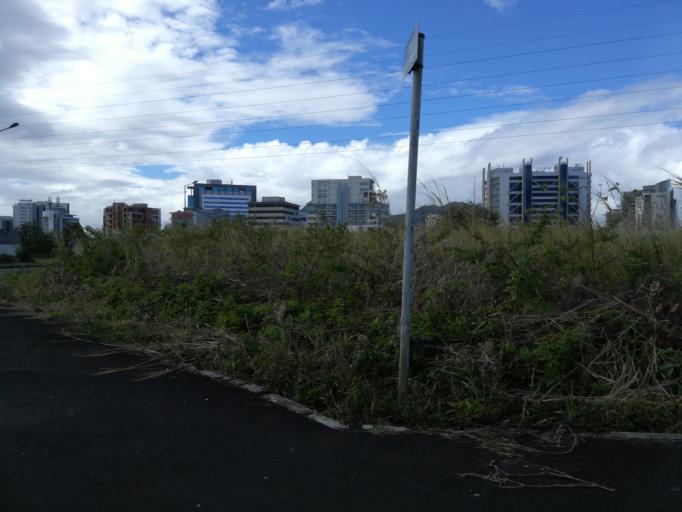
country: MU
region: Plaines Wilhems
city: Ebene
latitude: -20.2482
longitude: 57.4891
